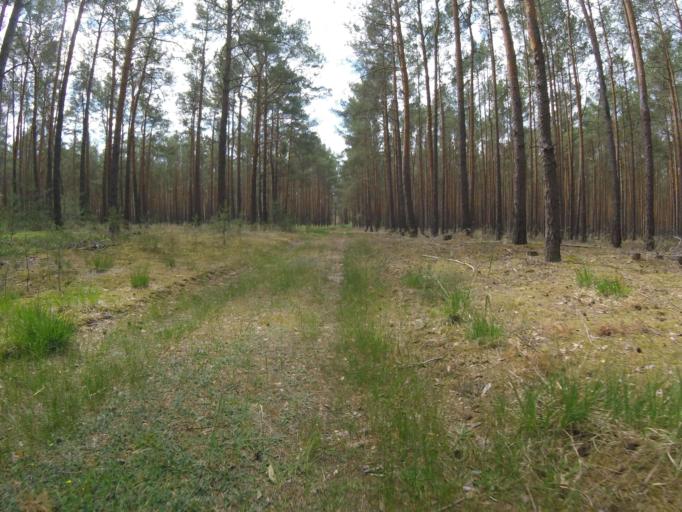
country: DE
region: Brandenburg
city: Halbe
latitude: 52.1050
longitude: 13.6615
